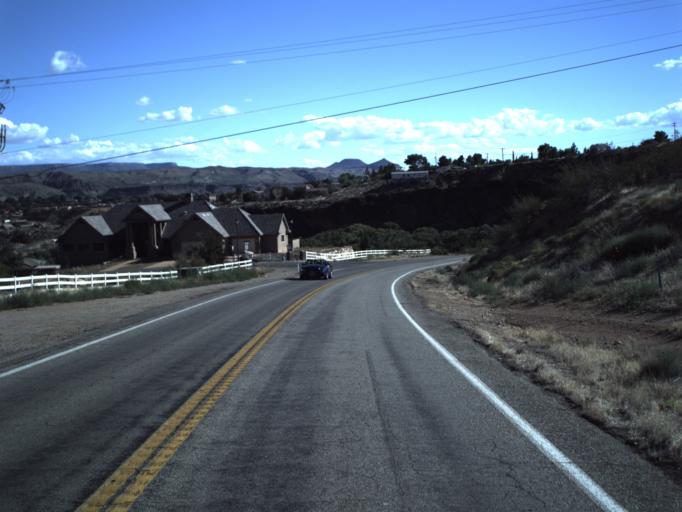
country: US
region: Utah
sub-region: Washington County
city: Toquerville
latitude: 37.2283
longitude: -113.2808
